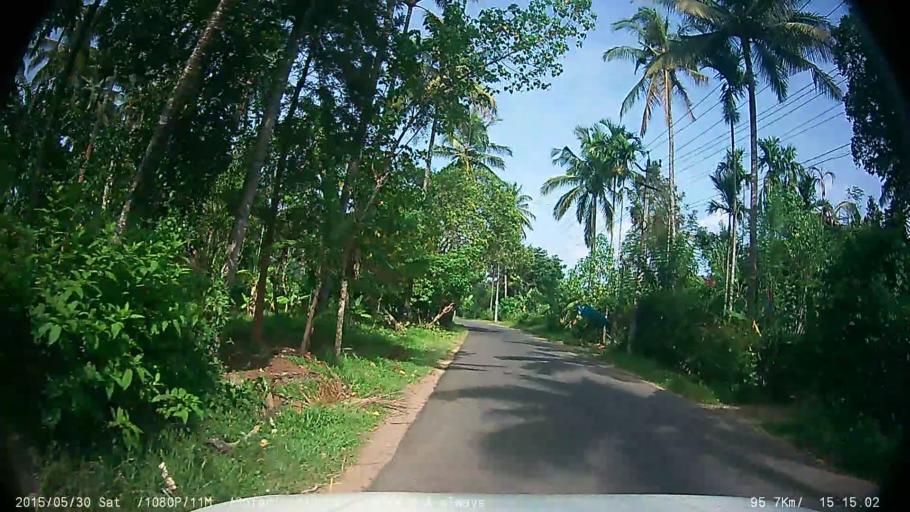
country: IN
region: Kerala
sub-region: Wayanad
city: Panamaram
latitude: 11.7818
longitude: 76.0470
